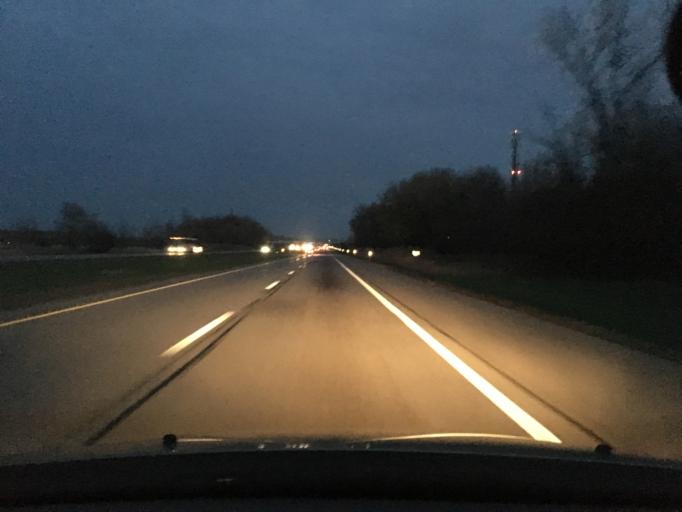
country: US
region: New York
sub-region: Ontario County
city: Victor
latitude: 42.9921
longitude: -77.3323
